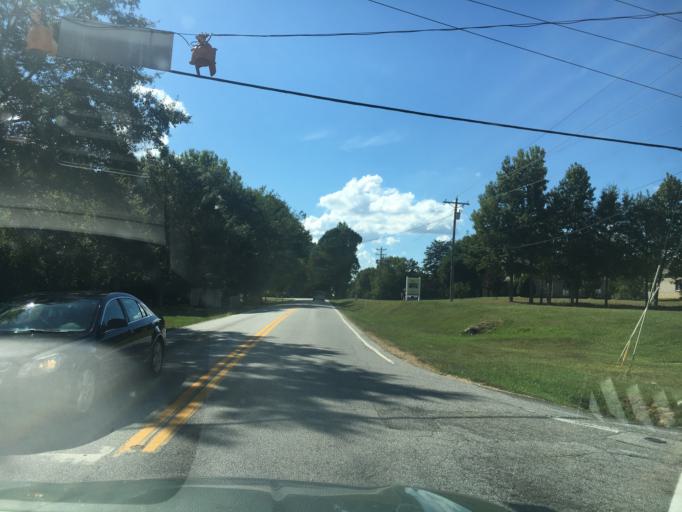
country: US
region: South Carolina
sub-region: Greenville County
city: Five Forks
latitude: 34.8226
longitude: -82.2286
